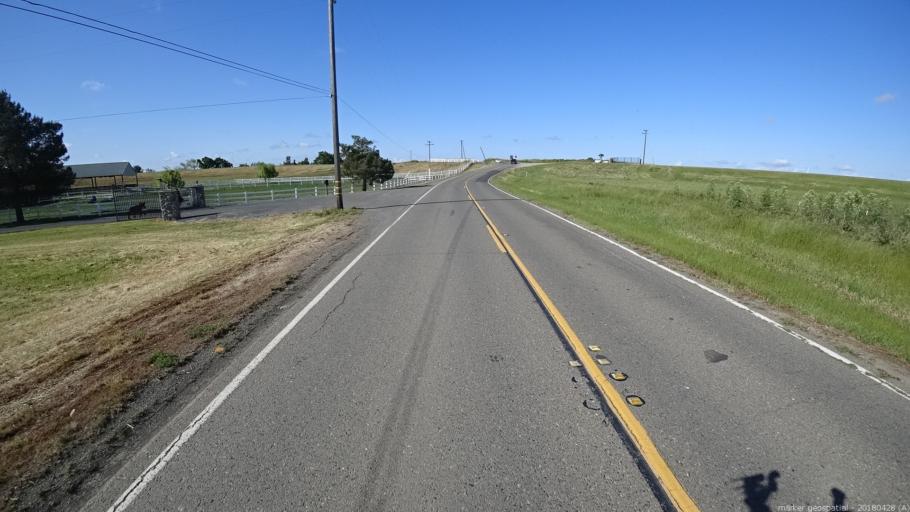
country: US
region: California
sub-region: Yolo County
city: West Sacramento
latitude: 38.5061
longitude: -121.5808
